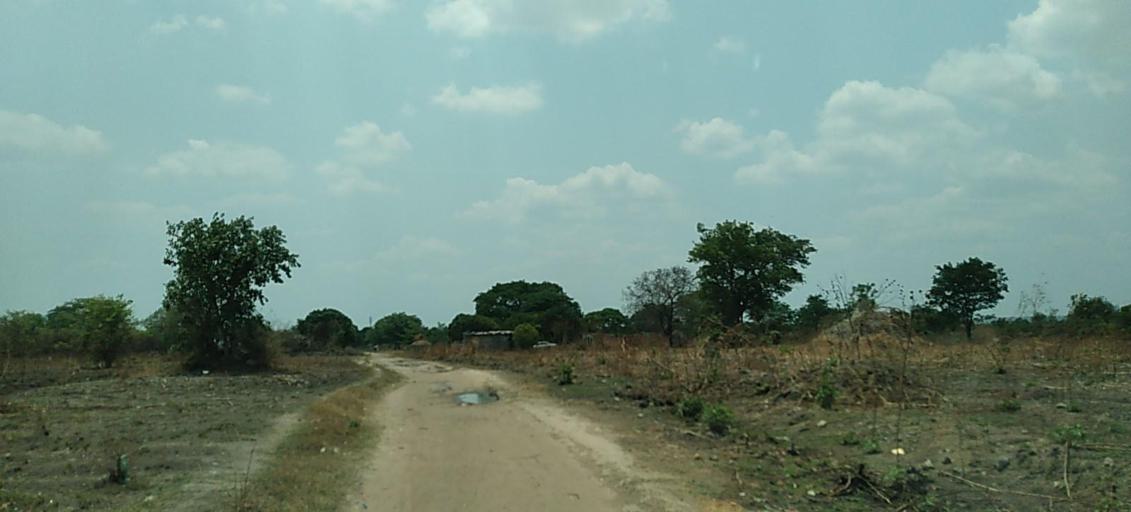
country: ZM
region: Copperbelt
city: Luanshya
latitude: -13.1001
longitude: 28.3015
